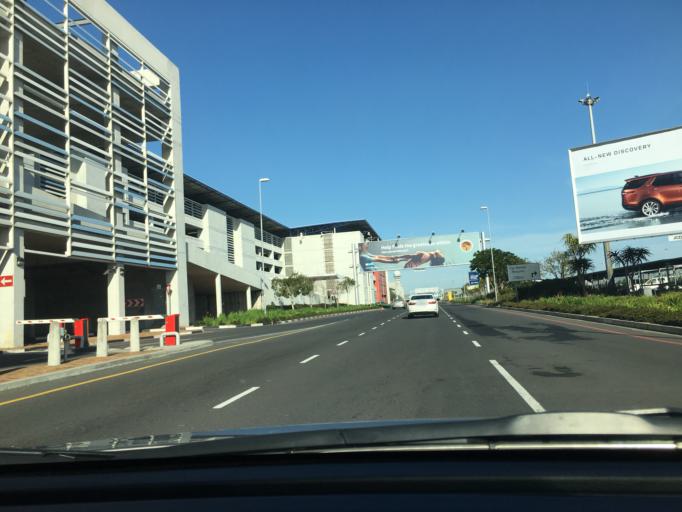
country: ZA
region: Western Cape
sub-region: City of Cape Town
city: Lansdowne
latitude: -33.9670
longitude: 18.5945
